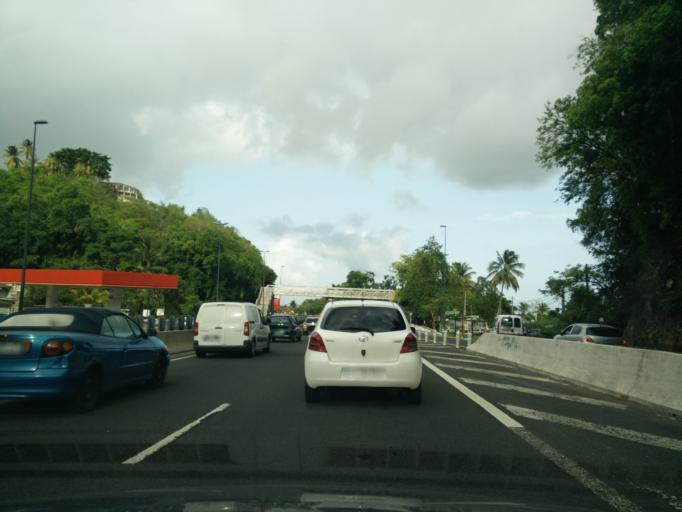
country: GP
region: Guadeloupe
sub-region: Guadeloupe
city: Le Gosier
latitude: 16.2181
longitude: -61.5122
